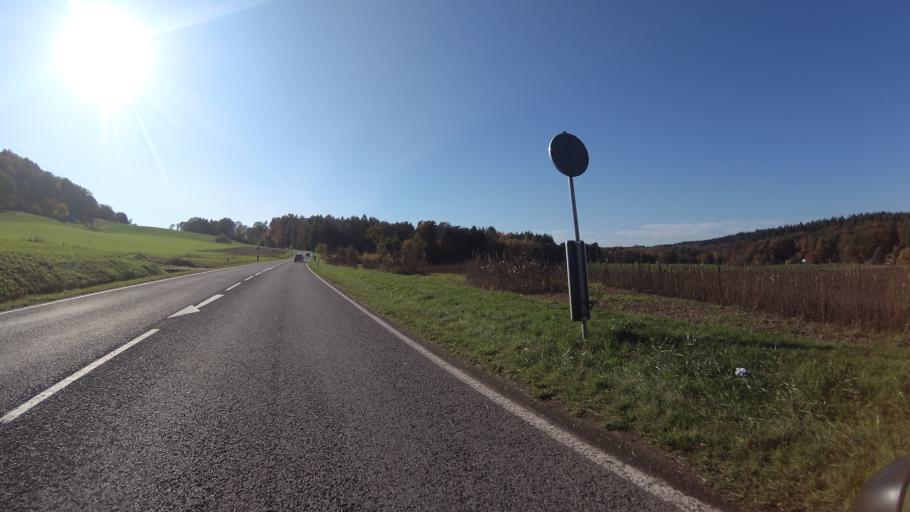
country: DE
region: Saarland
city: Losheim
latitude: 49.5046
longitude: 6.7364
